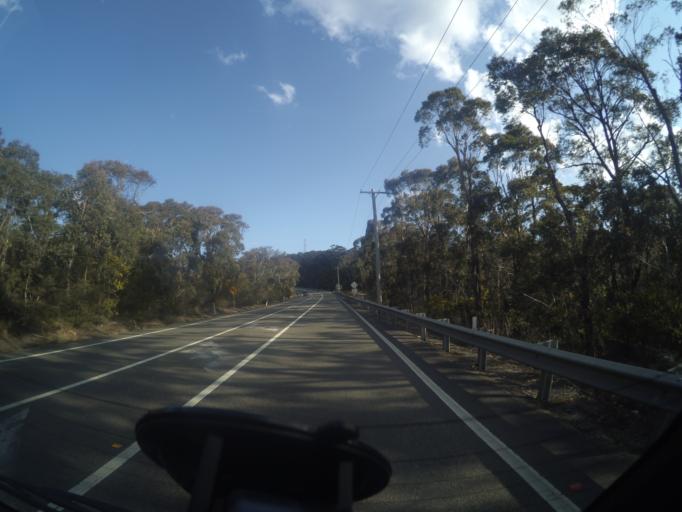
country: AU
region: New South Wales
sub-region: Blue Mountains Municipality
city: Katoomba
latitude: -33.6988
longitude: 150.2910
